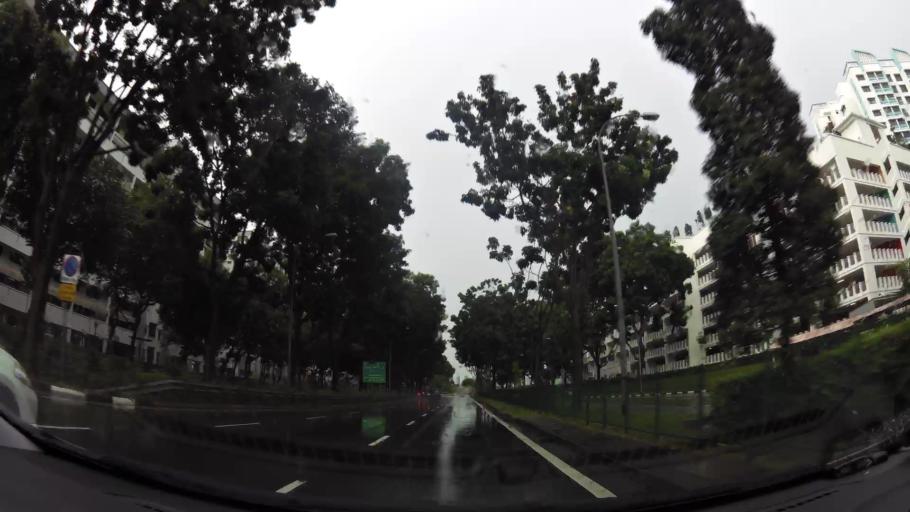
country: MY
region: Johor
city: Kampung Pasir Gudang Baru
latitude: 1.3807
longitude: 103.8902
